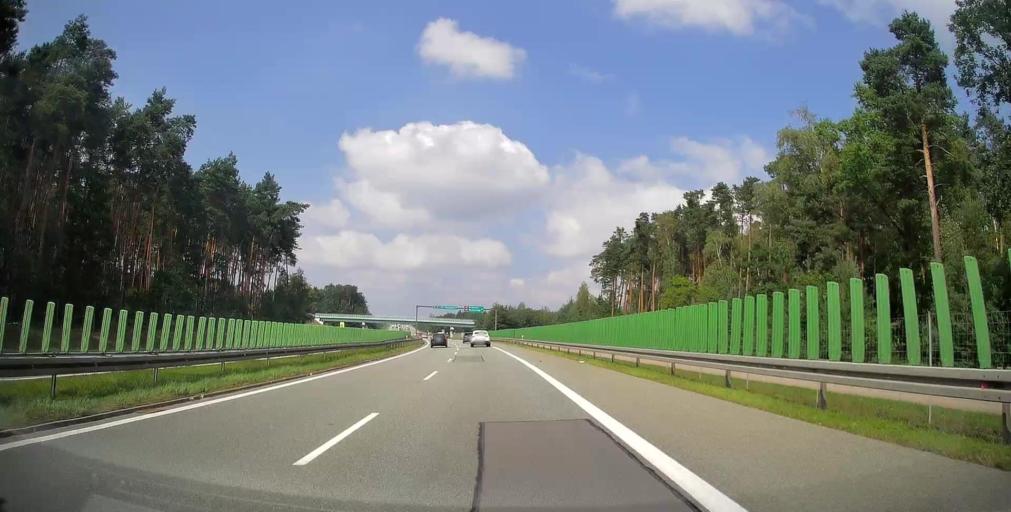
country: PL
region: Masovian Voivodeship
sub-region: Powiat bialobrzeski
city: Bialobrzegi
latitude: 51.6474
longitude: 20.9740
